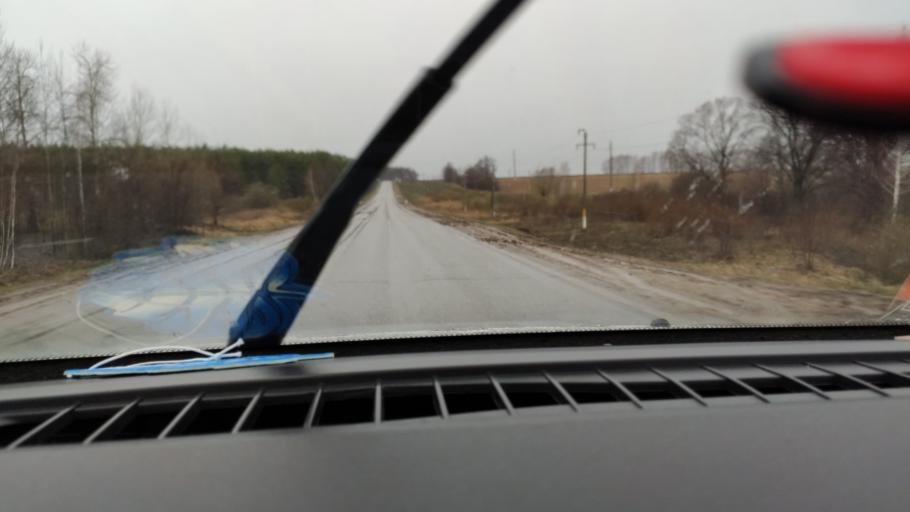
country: RU
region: Samara
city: Chelno-Vershiny
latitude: 54.6794
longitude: 51.0351
